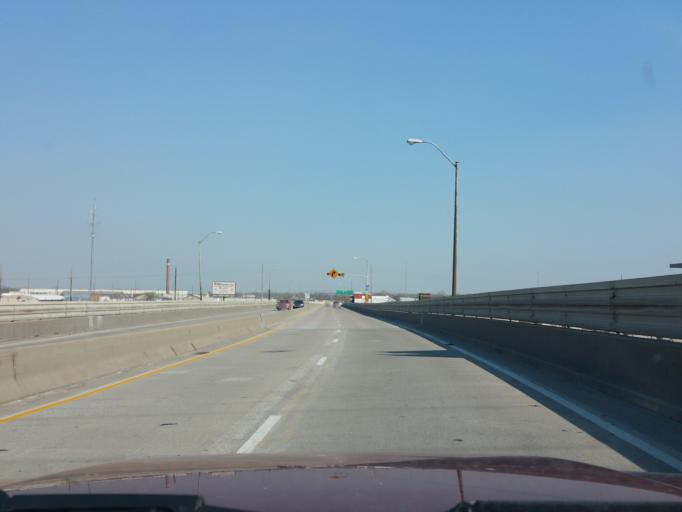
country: US
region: Kansas
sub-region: Shawnee County
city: Topeka
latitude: 39.0582
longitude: -95.6744
